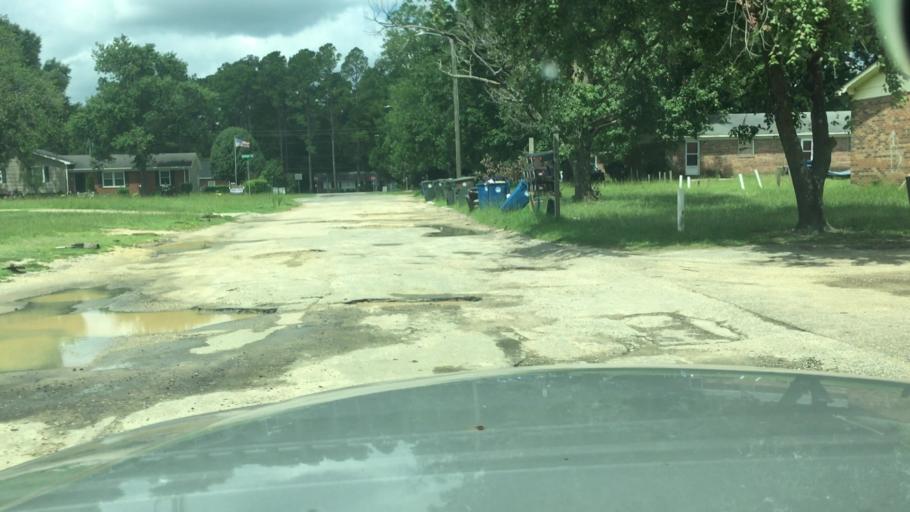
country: US
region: North Carolina
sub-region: Cumberland County
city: Hope Mills
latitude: 35.0359
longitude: -78.9955
